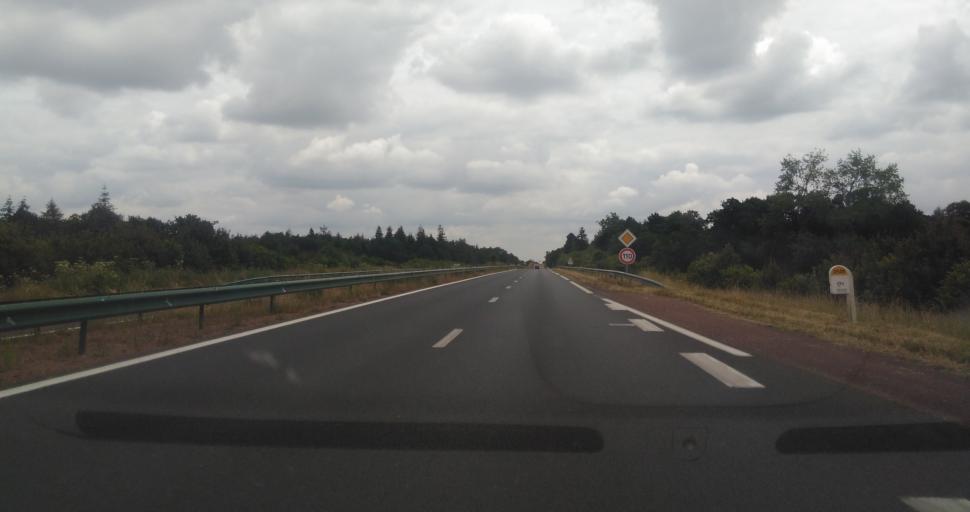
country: FR
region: Pays de la Loire
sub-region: Departement de la Vendee
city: Bournezeau
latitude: 46.6515
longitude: -1.2252
